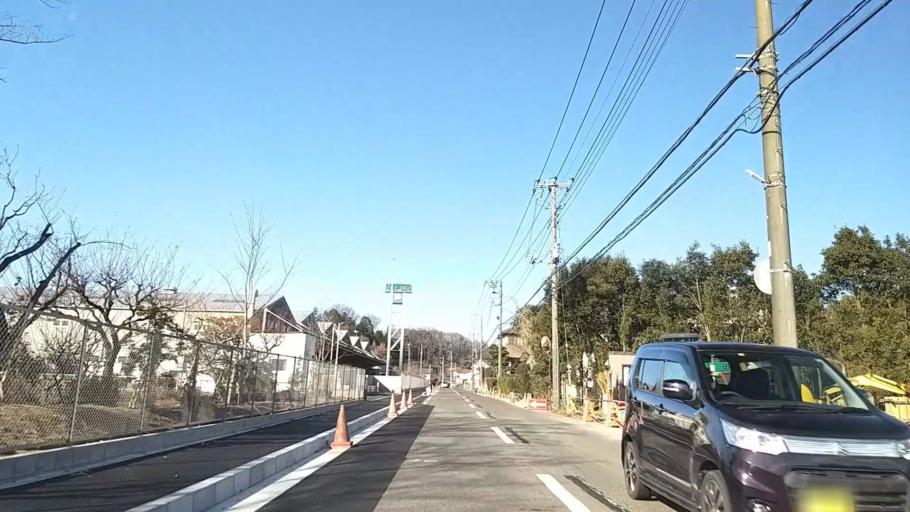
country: JP
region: Kanagawa
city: Atsugi
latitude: 35.4518
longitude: 139.3121
